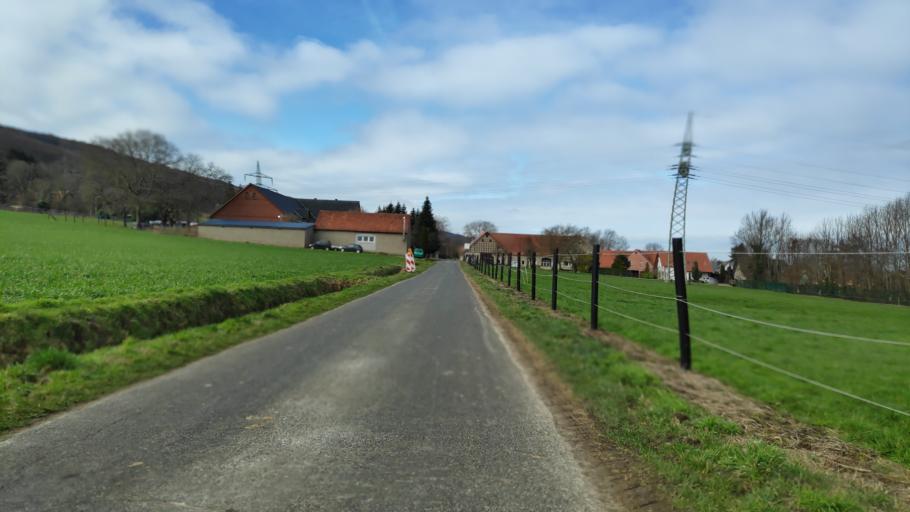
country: DE
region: North Rhine-Westphalia
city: Bad Oeynhausen
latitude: 52.2623
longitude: 8.8403
